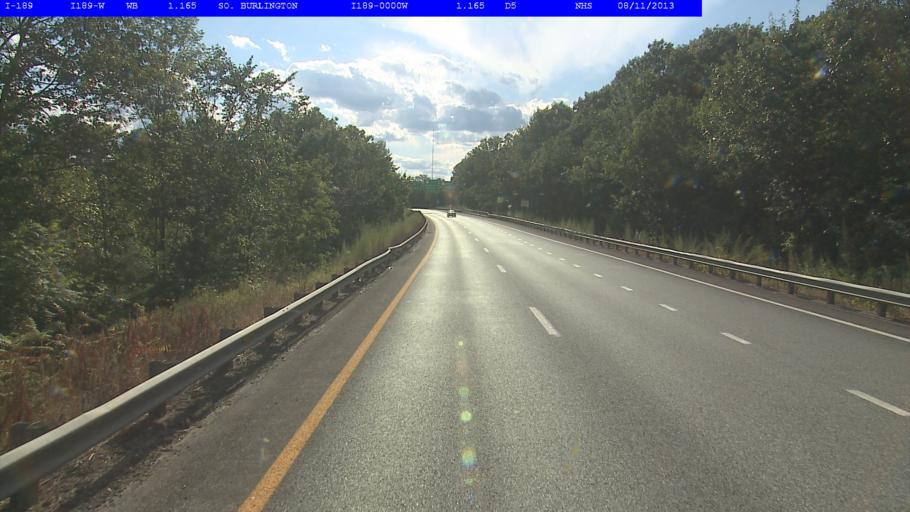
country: US
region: Vermont
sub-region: Chittenden County
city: South Burlington
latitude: 44.4519
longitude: -73.1870
